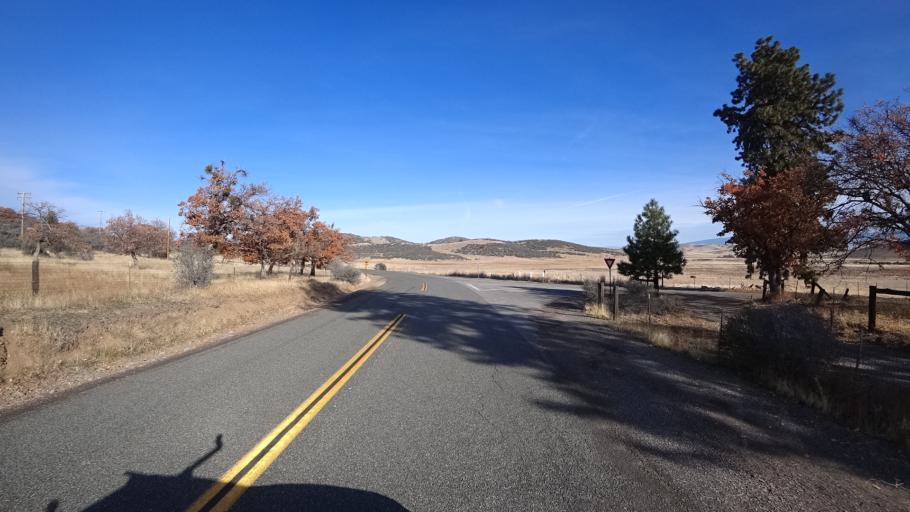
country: US
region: California
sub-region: Siskiyou County
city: Montague
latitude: 41.6392
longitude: -122.5747
